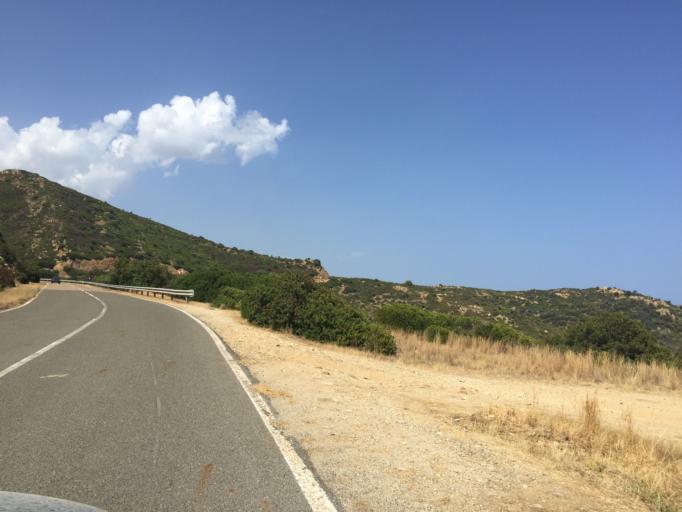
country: IT
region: Sardinia
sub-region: Provincia di Cagliari
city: Villasimius
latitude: 39.1477
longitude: 9.5591
